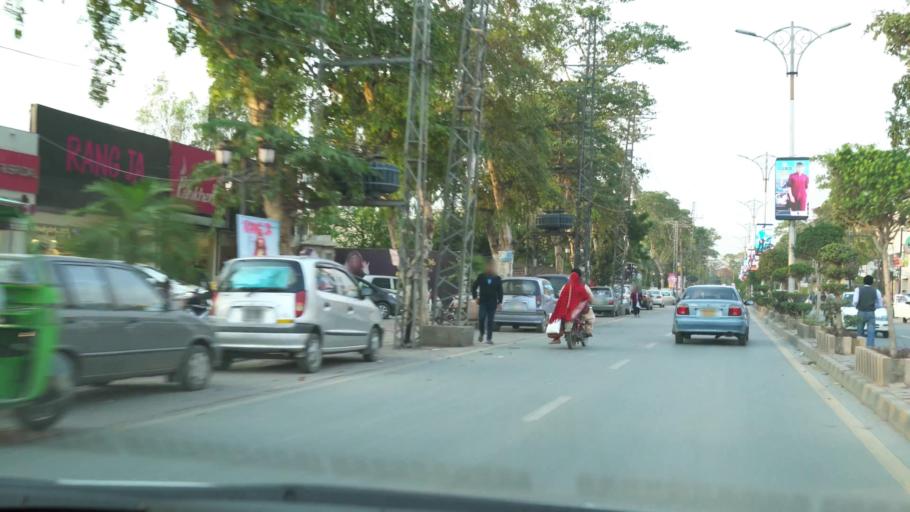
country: PK
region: Punjab
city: Lahore
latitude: 31.5138
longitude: 74.3513
